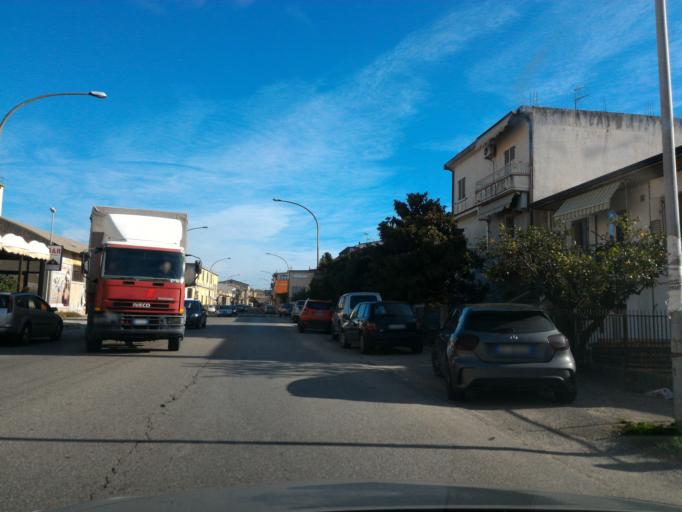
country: IT
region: Calabria
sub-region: Provincia di Catanzaro
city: Cropani Marina
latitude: 38.9234
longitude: 16.8081
